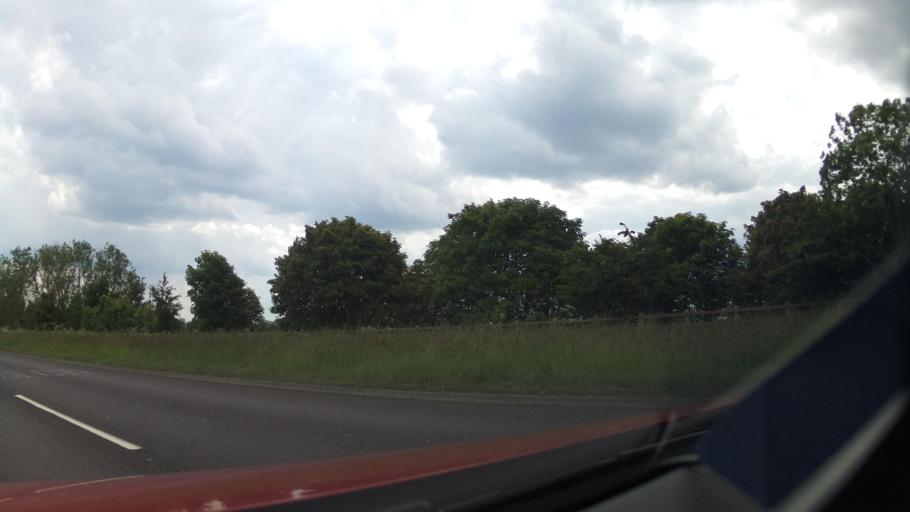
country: GB
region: England
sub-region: County Durham
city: Chester-le-Street
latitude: 54.9033
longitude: -1.5636
